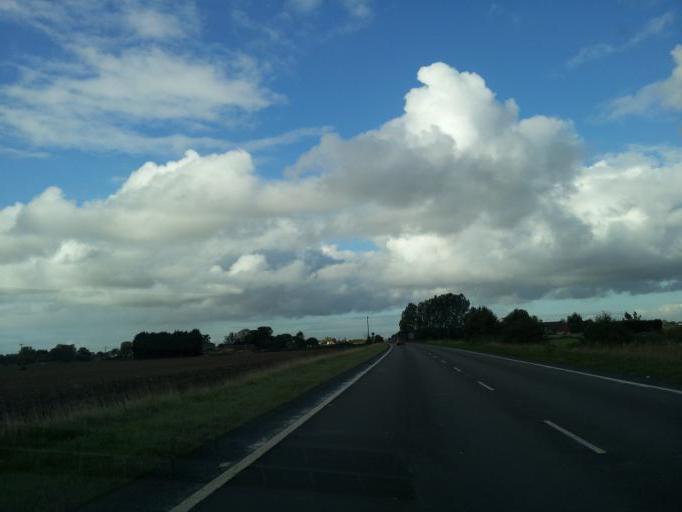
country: GB
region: England
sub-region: Norfolk
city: Terrington St Clement
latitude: 52.7466
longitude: 0.2826
